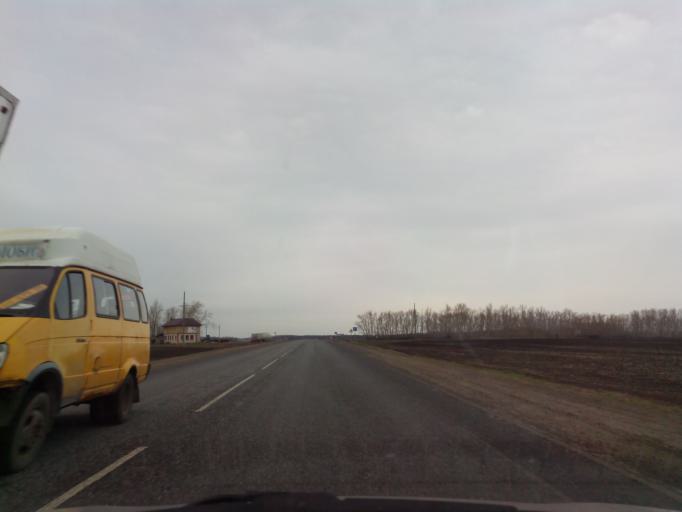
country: RU
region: Tambov
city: Zavoronezhskoye
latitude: 52.9860
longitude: 40.5600
